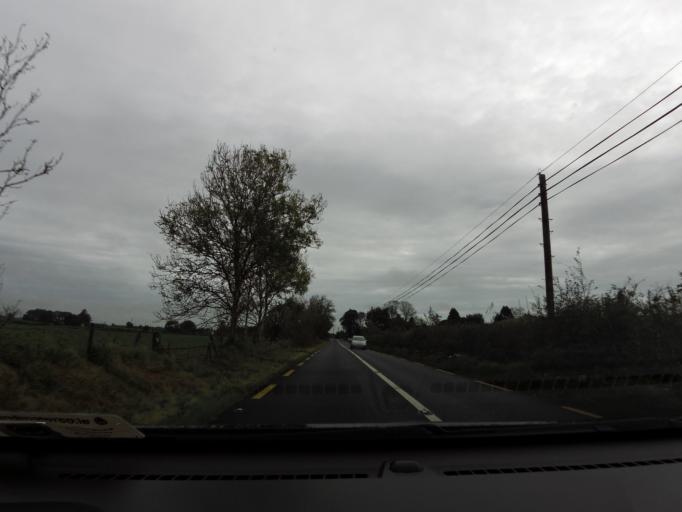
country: IE
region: Connaught
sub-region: County Galway
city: Tuam
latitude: 53.6004
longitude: -8.7624
